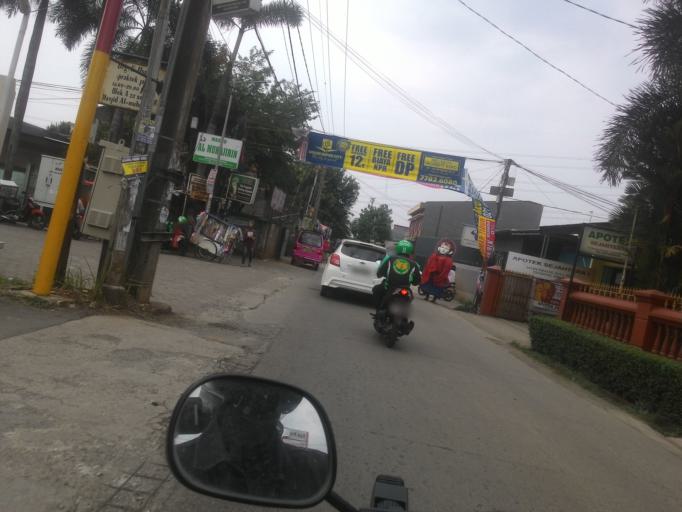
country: ID
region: West Java
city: Depok
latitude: -6.4234
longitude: 106.8376
